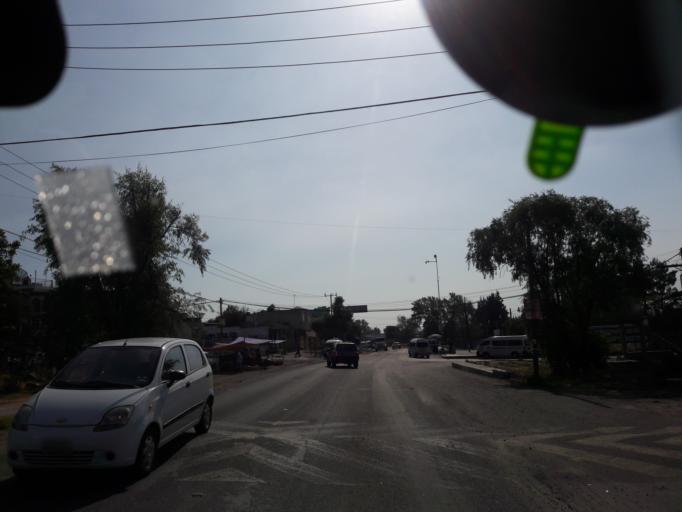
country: MX
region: Tlaxcala
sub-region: Ixtacuixtla de Mariano Matamoros
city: Santa Justina Ecatepec
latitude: 19.3087
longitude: -98.3553
